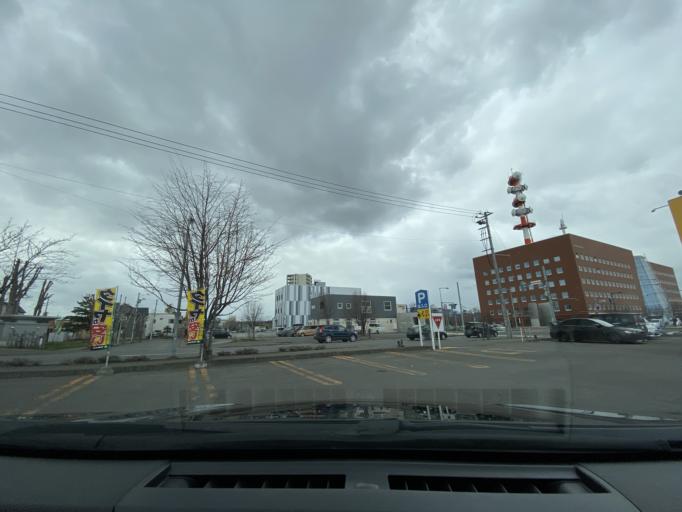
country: JP
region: Hokkaido
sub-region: Asahikawa-shi
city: Asahikawa
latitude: 43.7578
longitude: 142.3748
